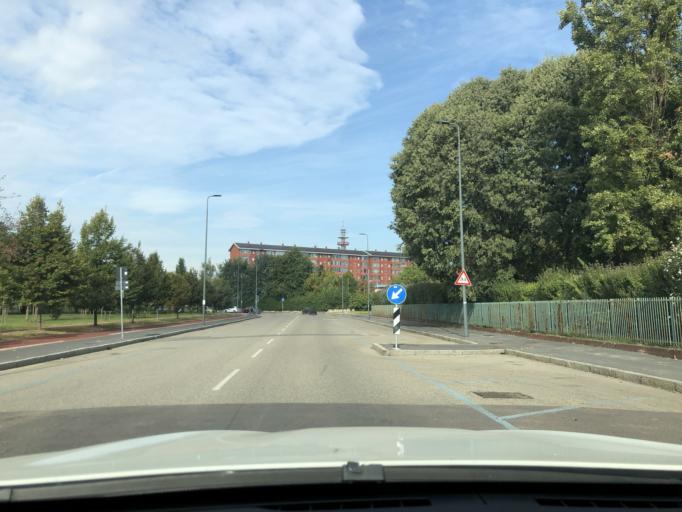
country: IT
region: Lombardy
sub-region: Citta metropolitana di Milano
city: Pero
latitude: 45.5034
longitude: 9.0988
